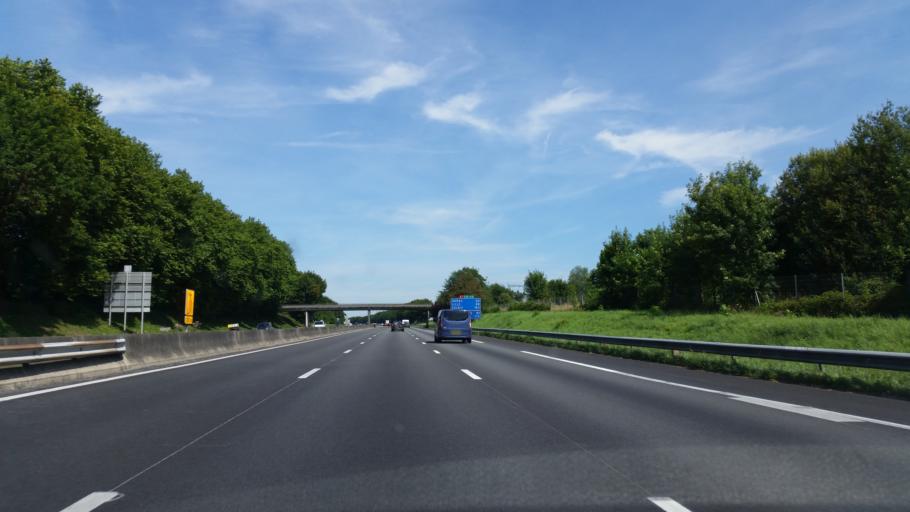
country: FR
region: Picardie
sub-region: Departement de la Somme
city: Chaulnes
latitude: 49.8942
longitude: 2.8431
